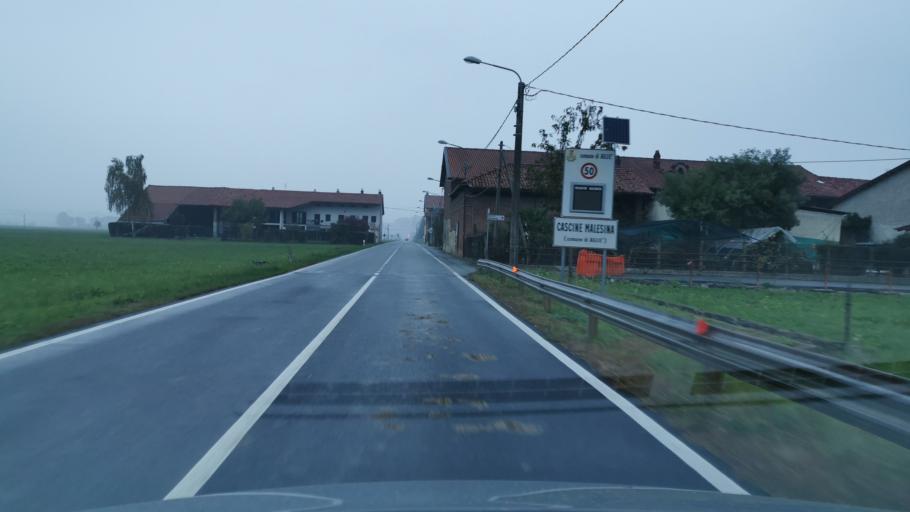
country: IT
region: Piedmont
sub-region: Provincia di Torino
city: Ciconio
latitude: 45.3468
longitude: 7.7659
